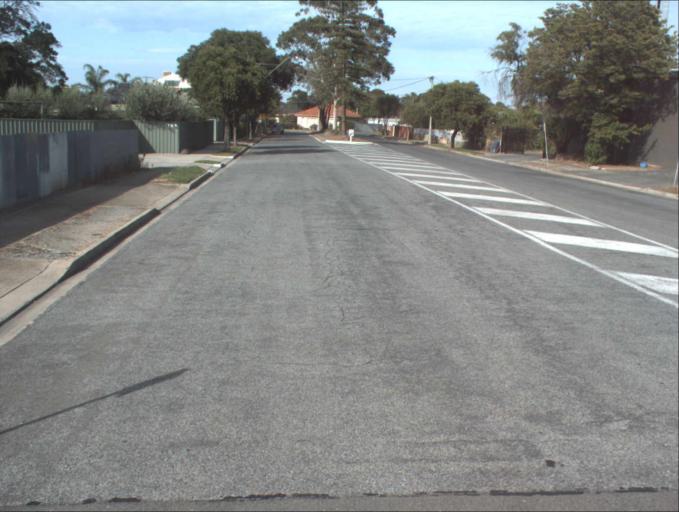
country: AU
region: South Australia
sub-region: Port Adelaide Enfield
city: Klemzig
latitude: -34.8731
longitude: 138.6189
